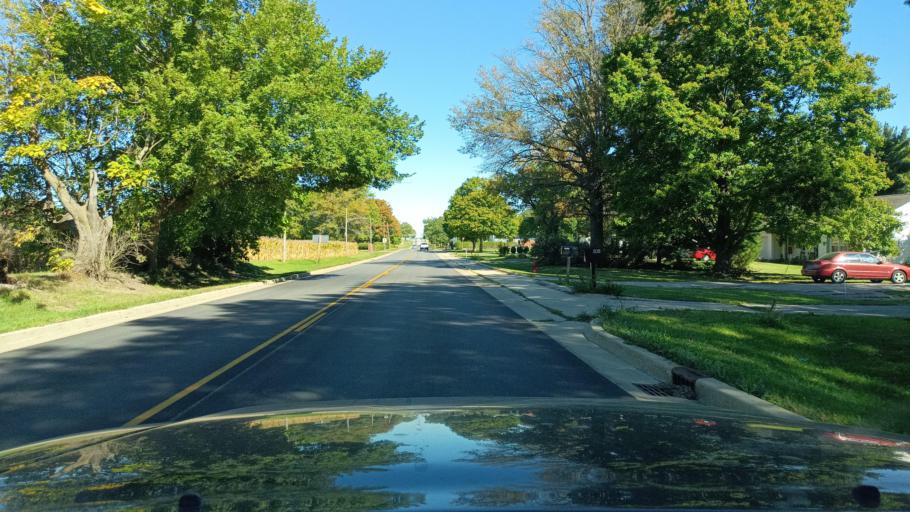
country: US
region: Illinois
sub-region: Champaign County
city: Philo
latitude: 40.0017
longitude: -88.1614
